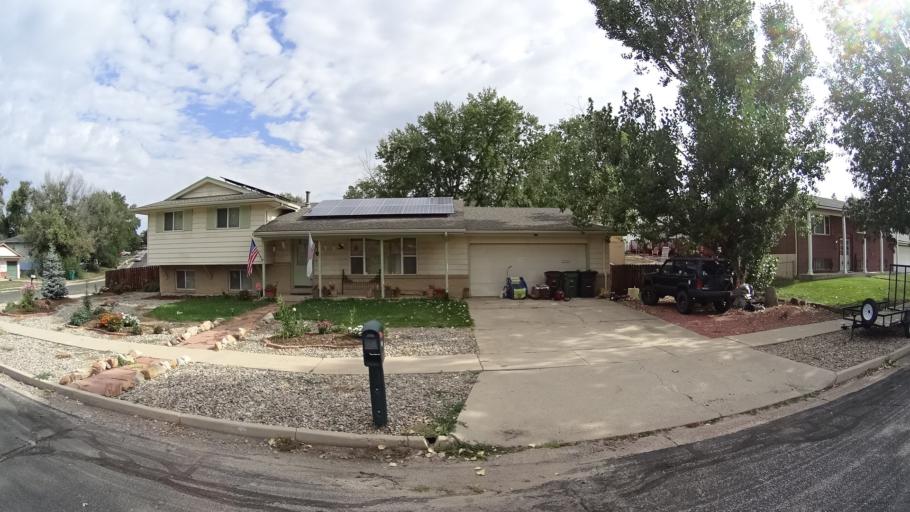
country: US
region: Colorado
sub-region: El Paso County
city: Cimarron Hills
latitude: 38.8414
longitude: -104.7541
